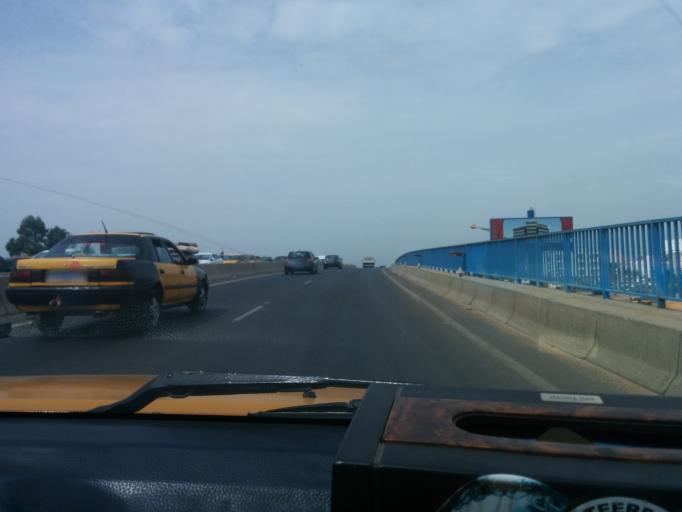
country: SN
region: Dakar
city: Mermoz Boabab
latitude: 14.7137
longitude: -17.4717
